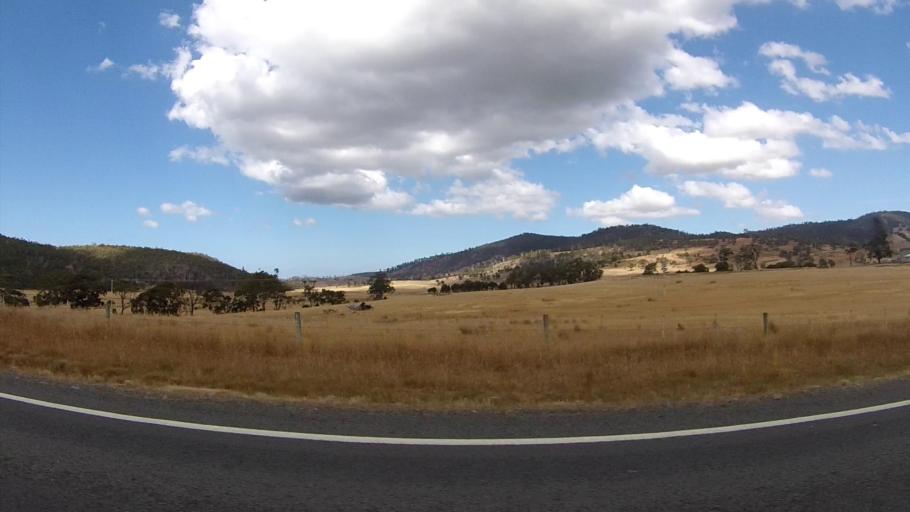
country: AU
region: Tasmania
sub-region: Sorell
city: Sorell
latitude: -42.6348
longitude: 147.6003
